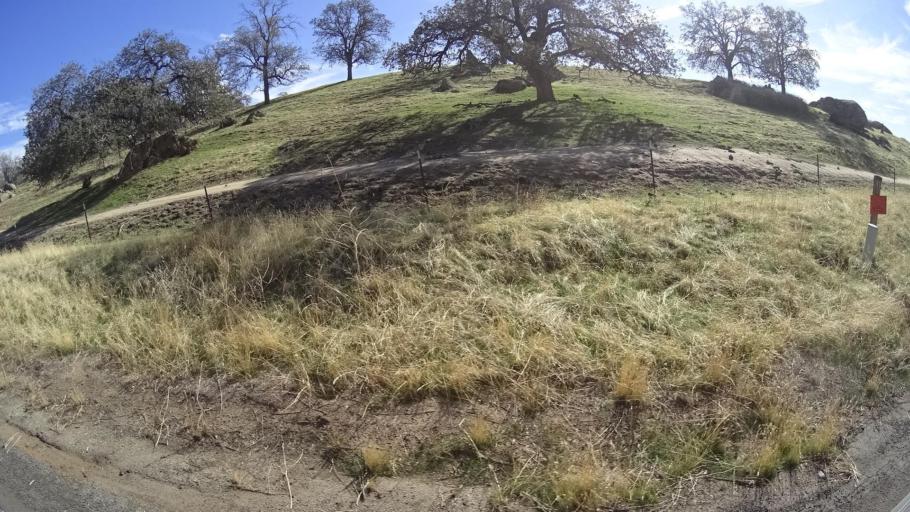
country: US
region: California
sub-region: Kern County
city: Oildale
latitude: 35.6266
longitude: -118.8464
